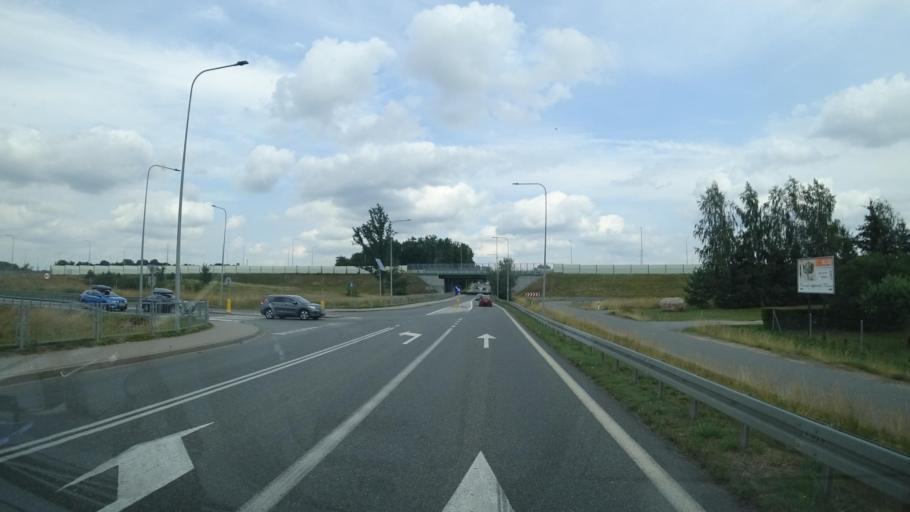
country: PL
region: Warmian-Masurian Voivodeship
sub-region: Powiat ostrodzki
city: Maldyty
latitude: 53.9027
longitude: 19.7279
